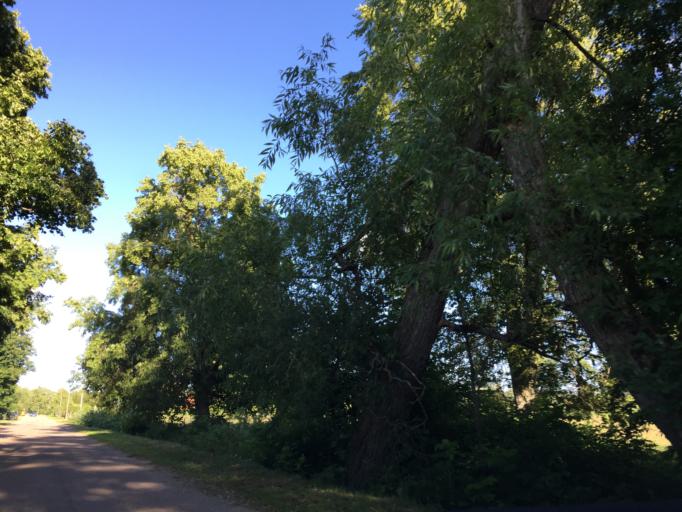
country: LV
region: Ventspils Rajons
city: Piltene
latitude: 57.3984
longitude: 21.8436
